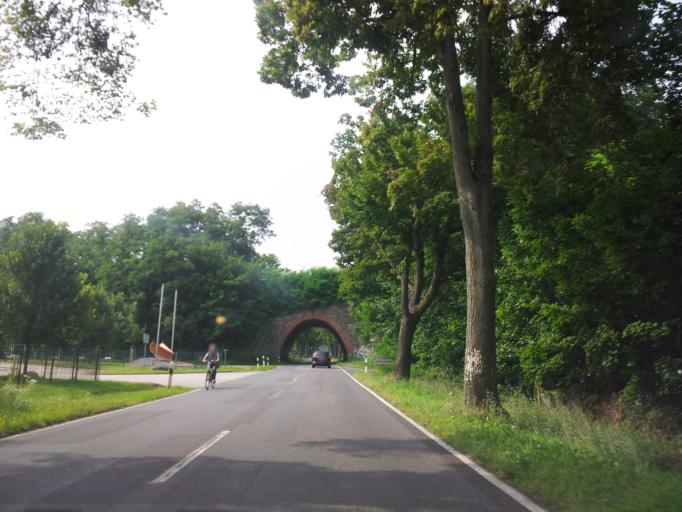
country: DE
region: Brandenburg
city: Belzig
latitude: 52.1359
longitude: 12.6127
